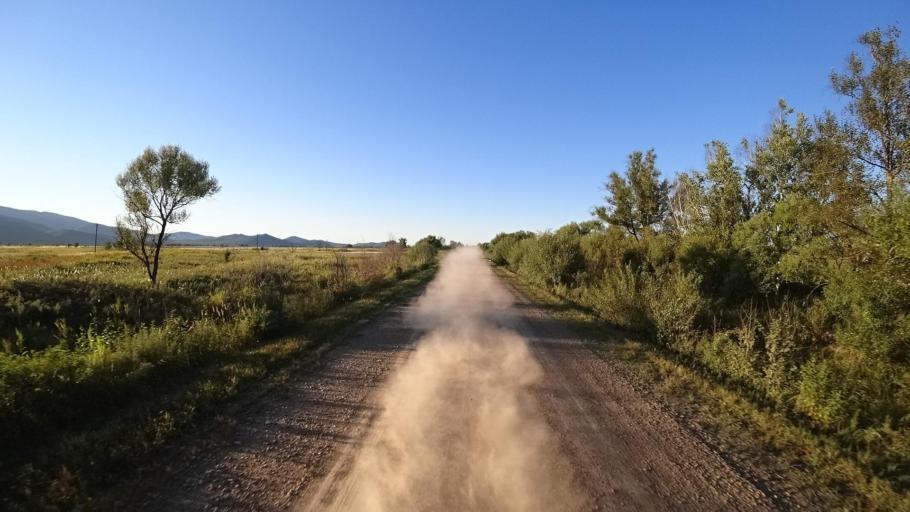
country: RU
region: Primorskiy
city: Kirovskiy
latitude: 44.7934
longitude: 133.6224
